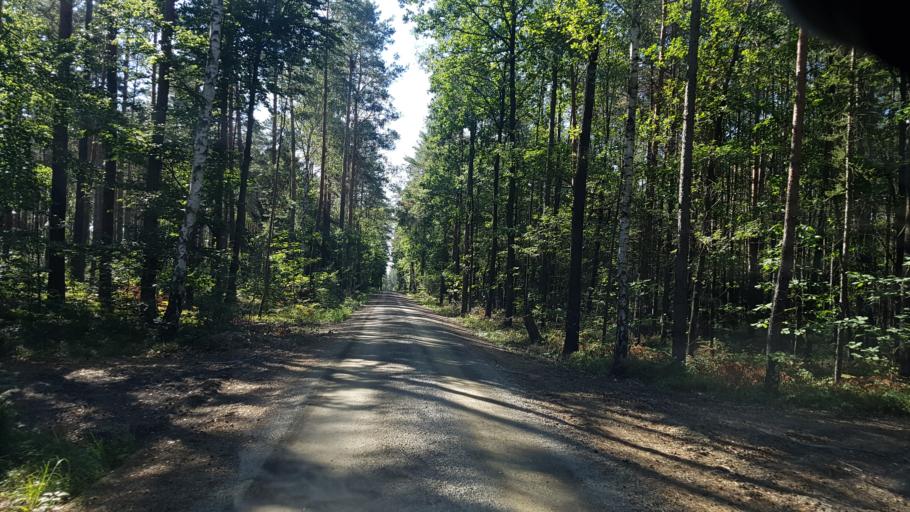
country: DE
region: Brandenburg
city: Ruckersdorf
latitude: 51.5418
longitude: 13.5812
